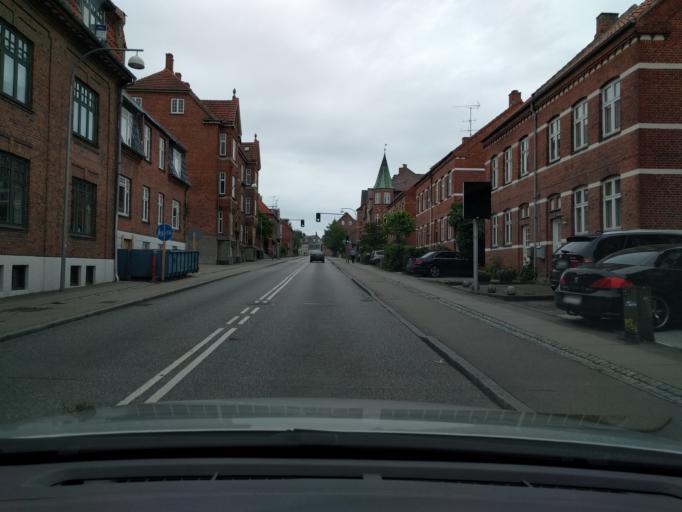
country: DK
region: Zealand
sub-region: Roskilde Kommune
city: Roskilde
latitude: 55.6396
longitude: 12.0728
